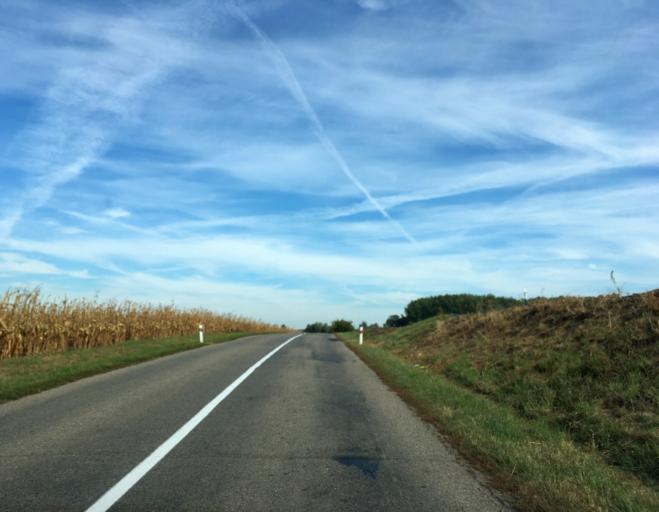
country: SK
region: Nitriansky
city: Svodin
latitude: 48.0012
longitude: 18.4121
